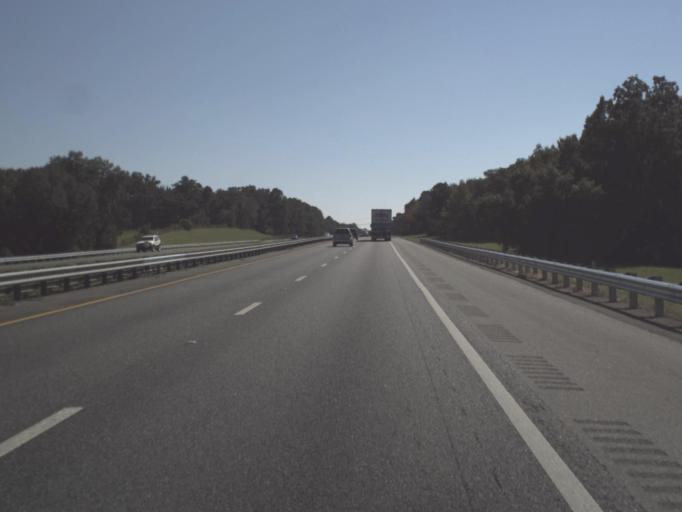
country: US
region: Florida
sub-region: Sumter County
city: Wildwood
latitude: 28.8224
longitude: -82.0233
